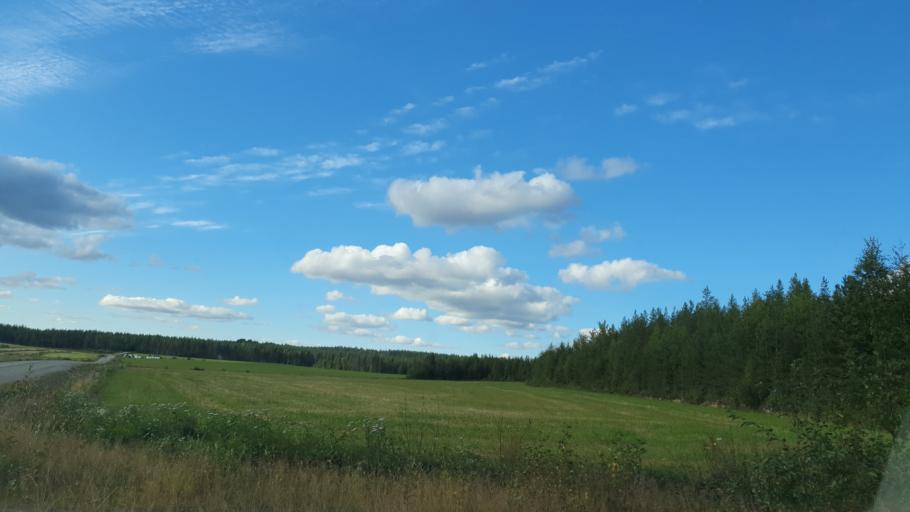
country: FI
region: Kainuu
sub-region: Kehys-Kainuu
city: Kuhmo
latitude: 64.1826
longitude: 29.4050
